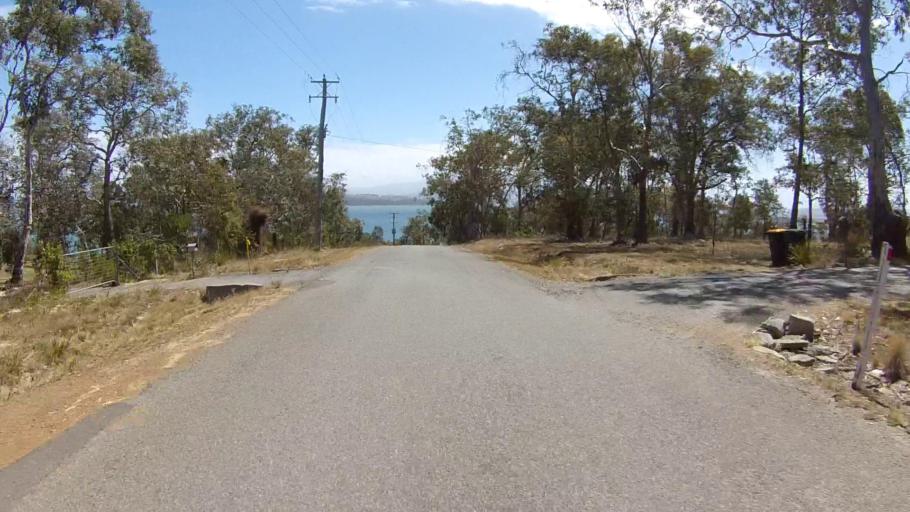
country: AU
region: Tasmania
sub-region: Clarence
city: Sandford
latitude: -42.9996
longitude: 147.4741
